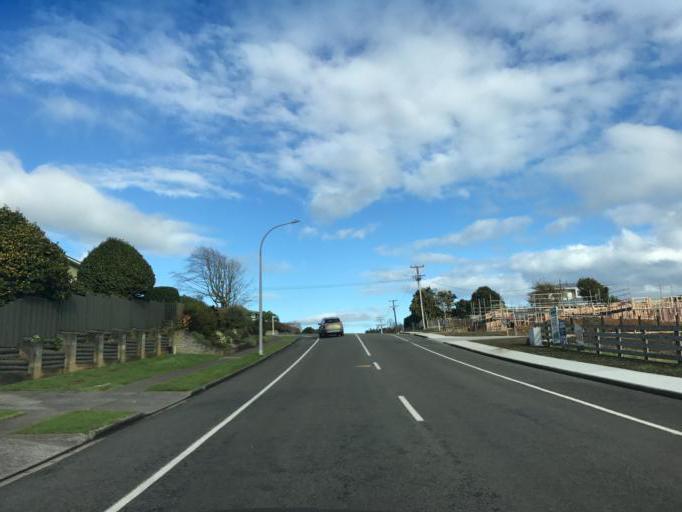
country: NZ
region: Taranaki
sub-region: South Taranaki District
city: Hawera
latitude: -39.5757
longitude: 174.2662
